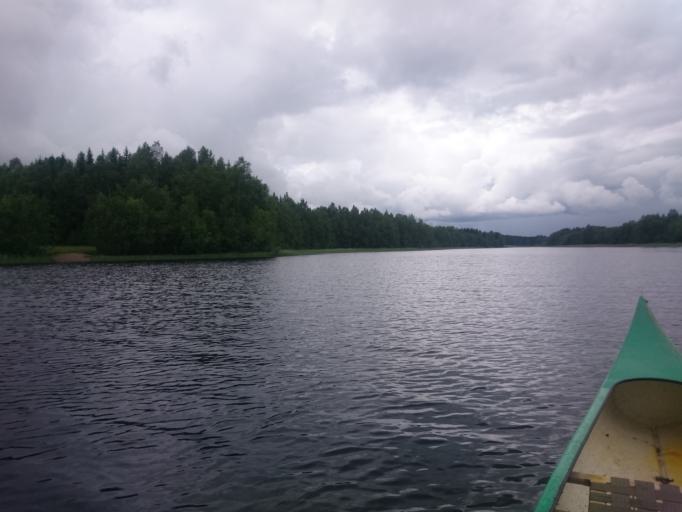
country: SE
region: Vaesternorrland
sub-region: OErnskoeldsviks Kommun
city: Ornskoldsvik
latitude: 63.6465
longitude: 18.6222
